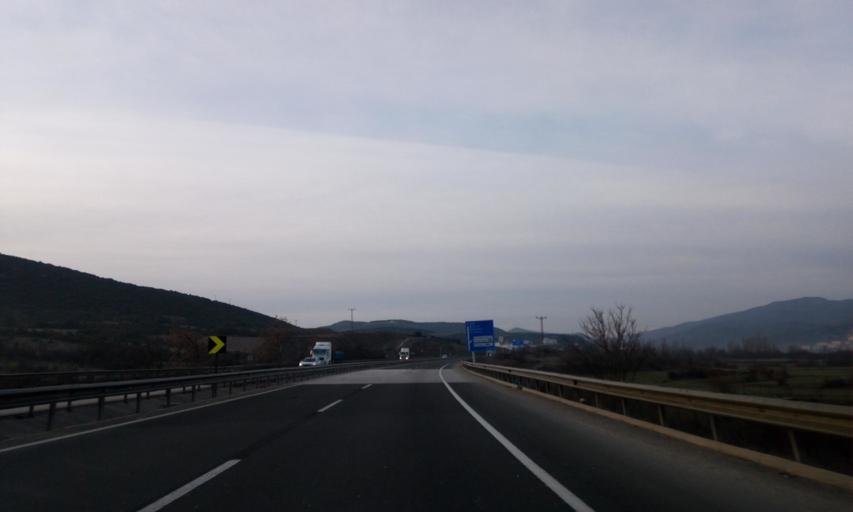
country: TR
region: Bilecik
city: Bilecik
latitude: 40.1413
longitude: 30.0261
